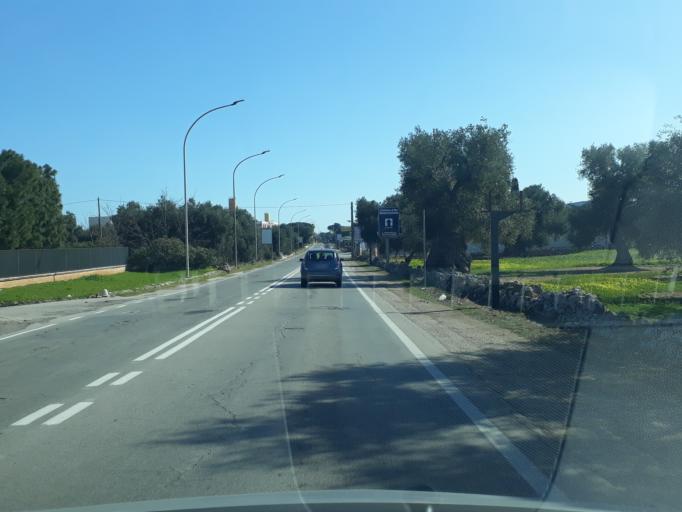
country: IT
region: Apulia
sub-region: Provincia di Bari
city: Monopoli
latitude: 40.9666
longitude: 17.2722
